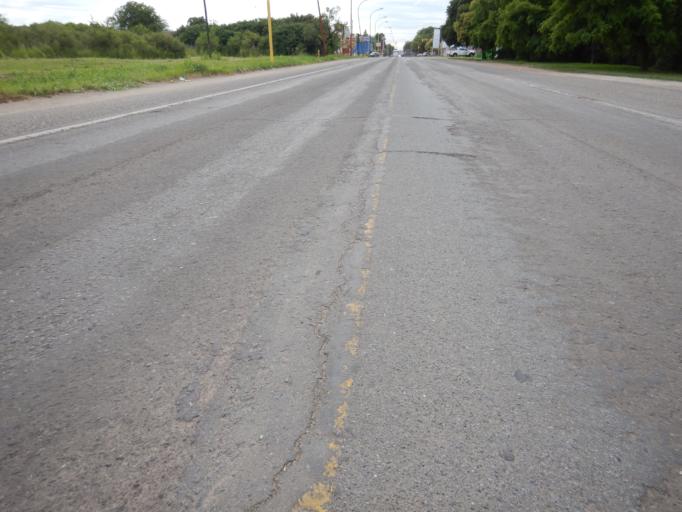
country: AR
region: Santa Fe
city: Canada de Gomez
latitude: -32.8088
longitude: -61.4036
